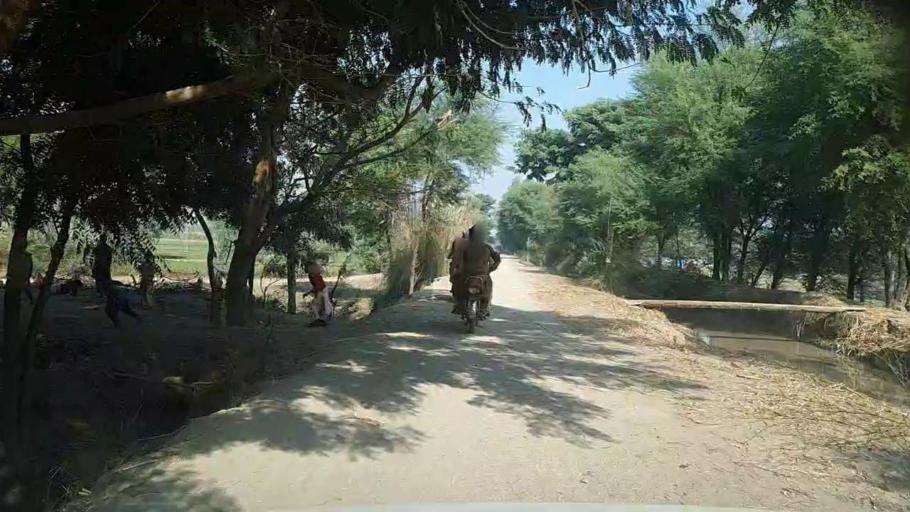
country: PK
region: Sindh
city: Karaundi
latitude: 26.9626
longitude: 68.4213
